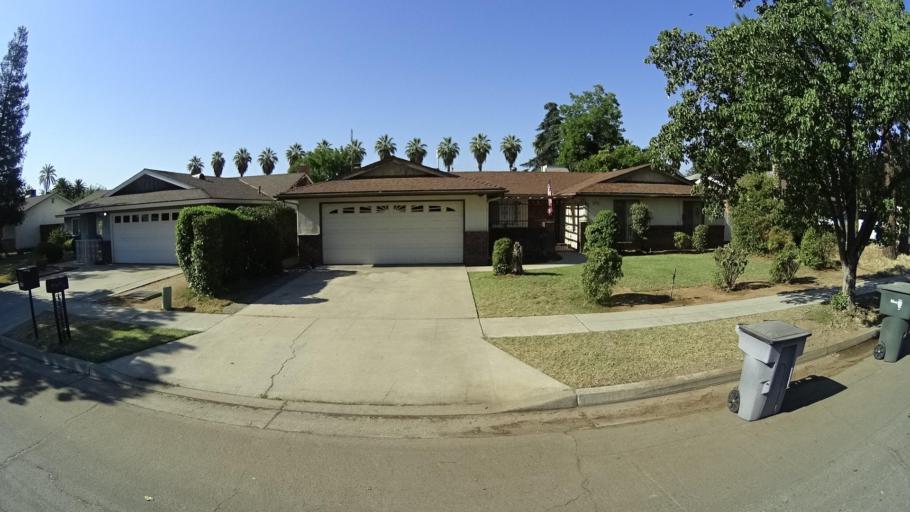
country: US
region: California
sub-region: Fresno County
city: Sunnyside
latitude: 36.7442
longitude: -119.7194
